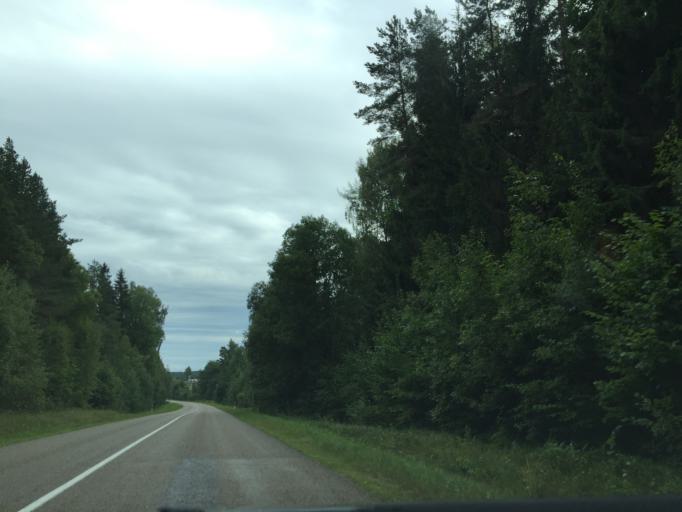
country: LV
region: Dagda
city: Dagda
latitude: 56.1846
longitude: 27.3741
